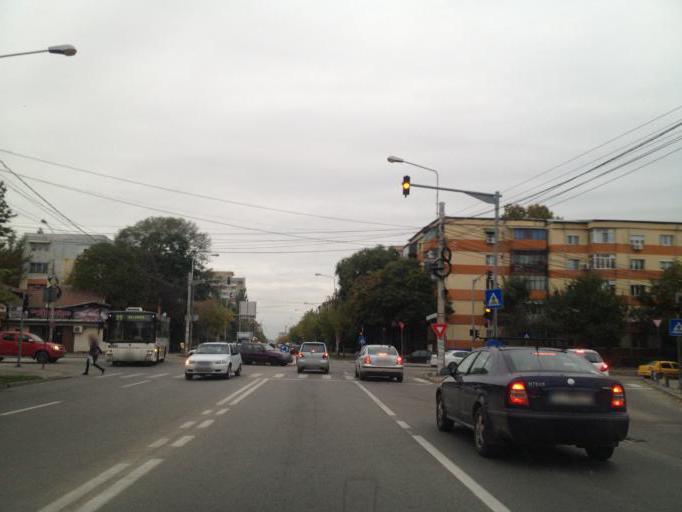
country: RO
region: Dolj
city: Craiova
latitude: 44.3289
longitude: 23.8132
